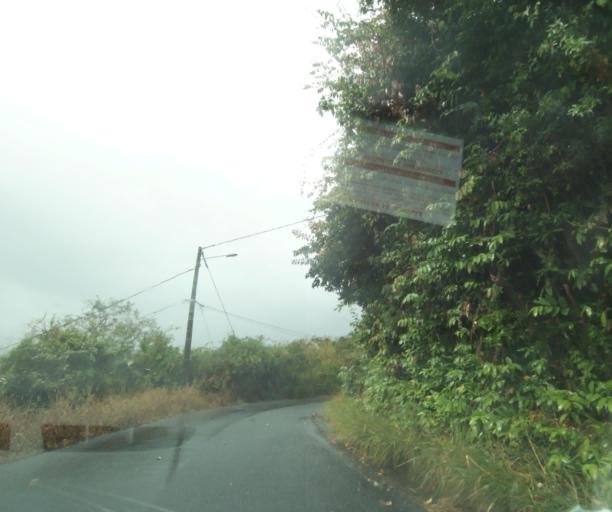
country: RE
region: Reunion
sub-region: Reunion
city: La Possession
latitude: -20.9790
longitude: 55.3348
